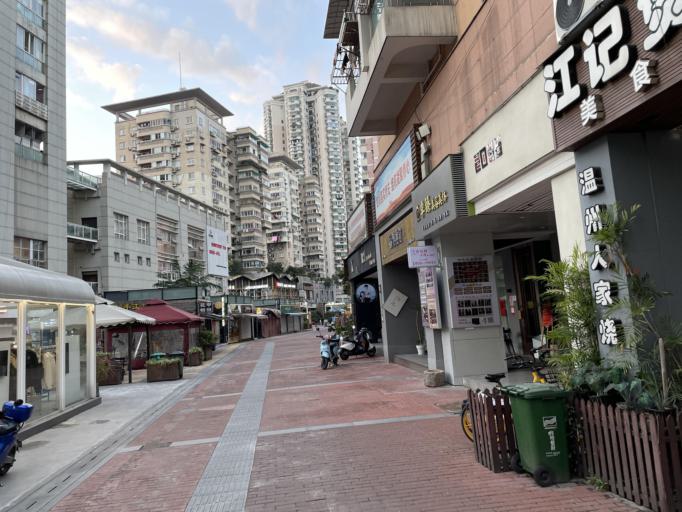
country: CN
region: Zhejiang Sheng
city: Wuma
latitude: 28.0112
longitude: 120.6619
